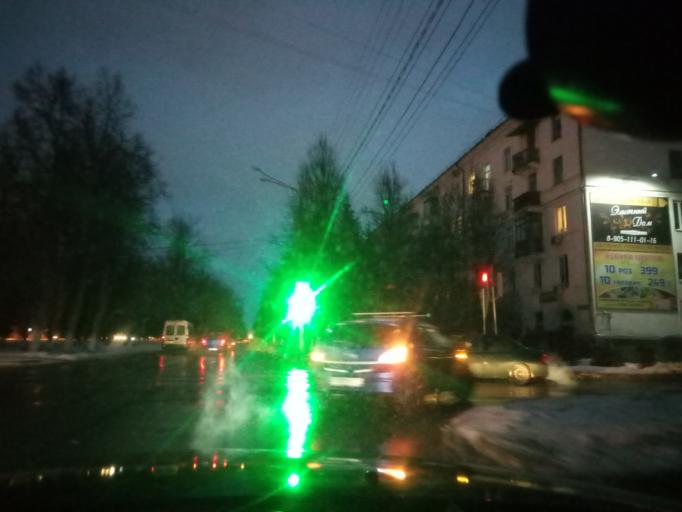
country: RU
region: Tula
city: Novomoskovsk
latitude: 54.0071
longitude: 38.2969
